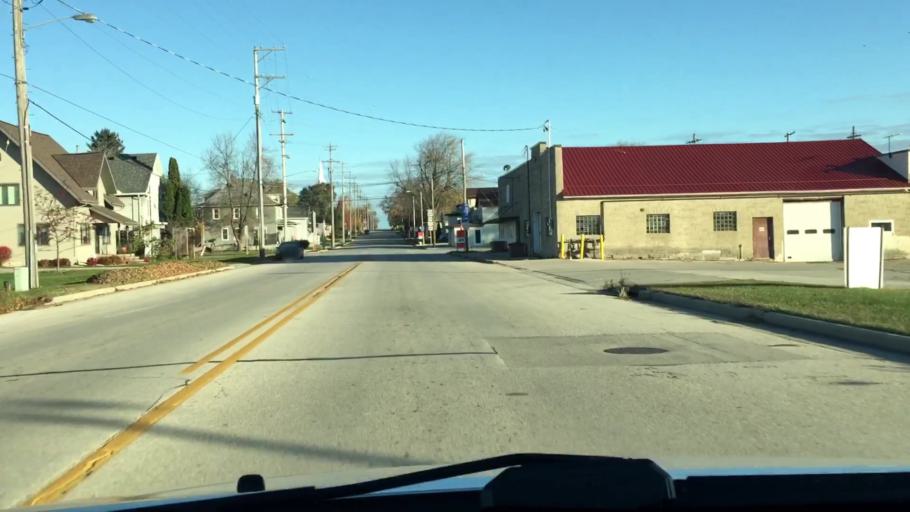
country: US
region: Wisconsin
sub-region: Dodge County
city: Lomira
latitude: 43.5863
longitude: -88.4501
